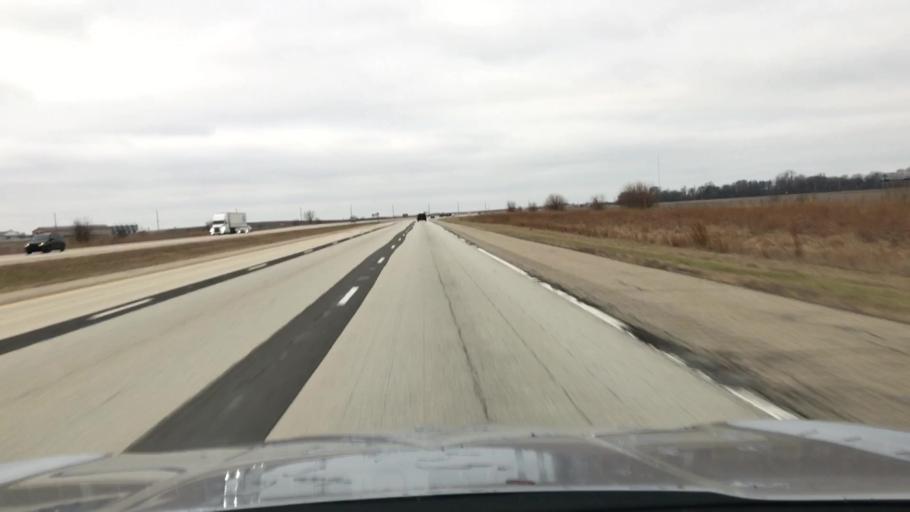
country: US
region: Illinois
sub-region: Sangamon County
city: Williamsville
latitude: 40.0095
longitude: -89.5004
